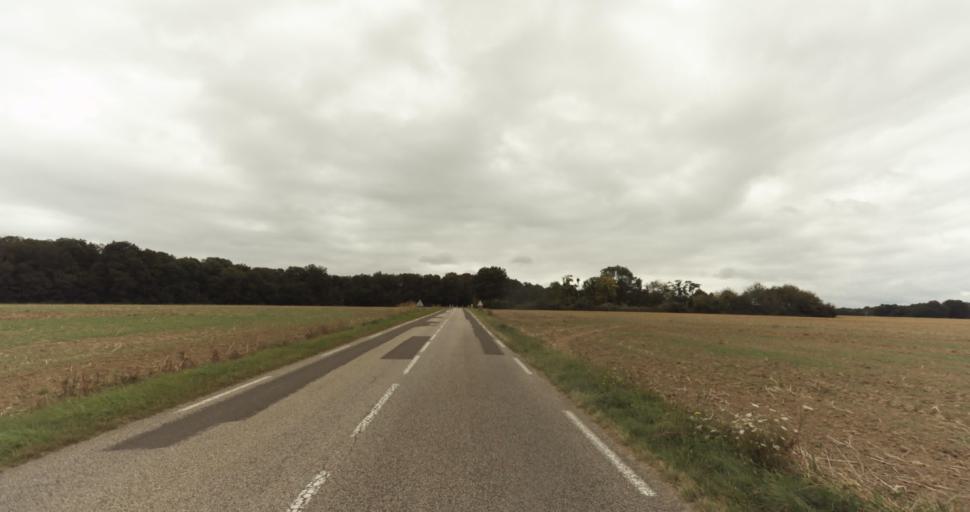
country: FR
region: Haute-Normandie
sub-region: Departement de l'Eure
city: Menilles
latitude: 49.0356
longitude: 1.2898
